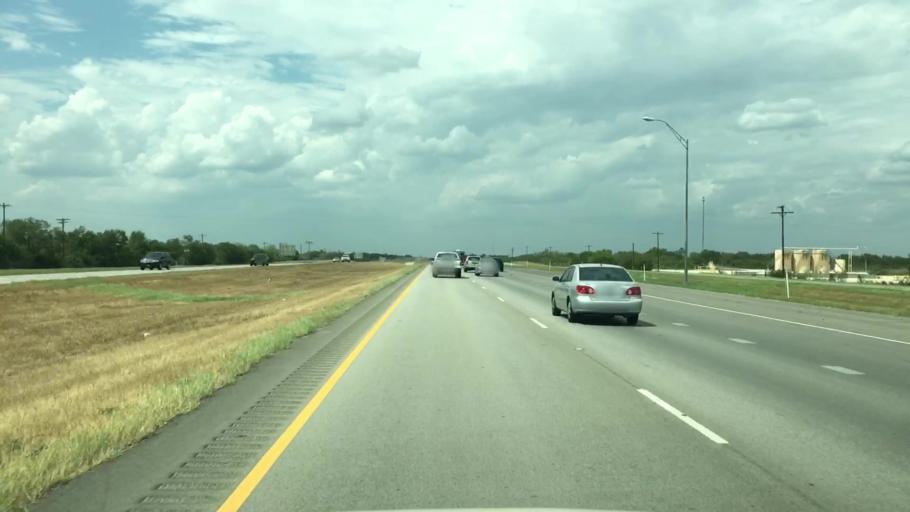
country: US
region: Texas
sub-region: Live Oak County
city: Three Rivers
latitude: 28.5359
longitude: -98.1891
